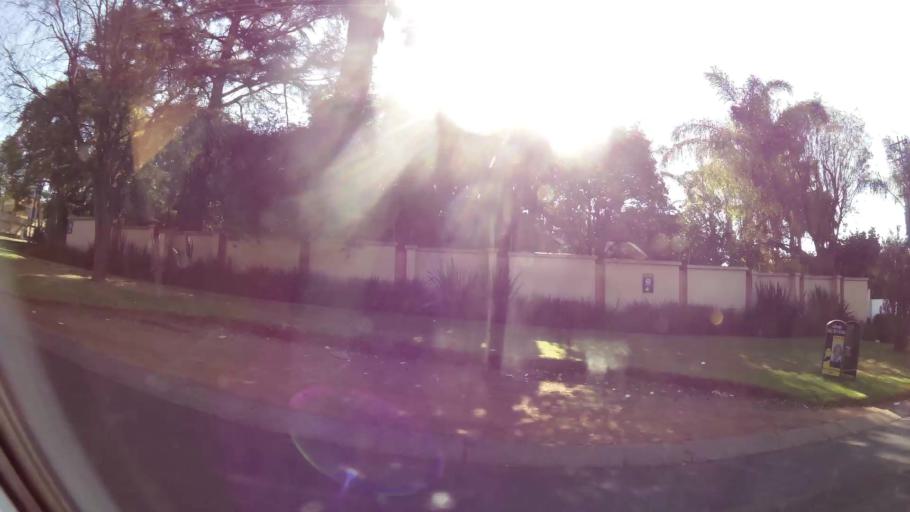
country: ZA
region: Gauteng
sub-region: City of Tshwane Metropolitan Municipality
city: Pretoria
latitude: -25.7946
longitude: 28.2417
